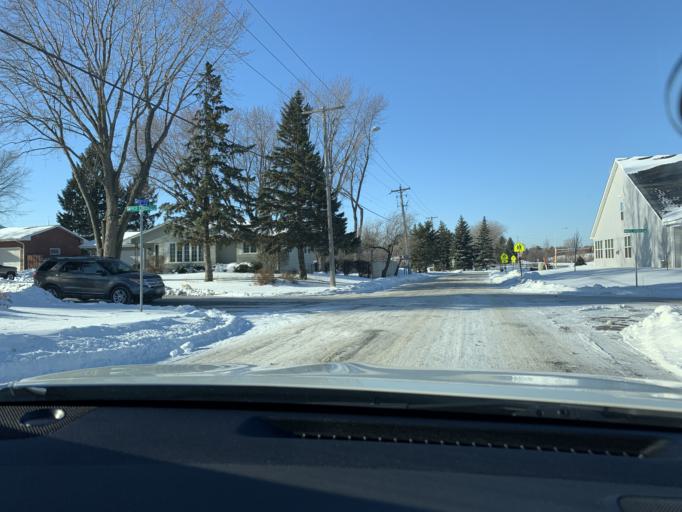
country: US
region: Minnesota
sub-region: Anoka County
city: Fridley
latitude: 45.0933
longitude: -93.2612
